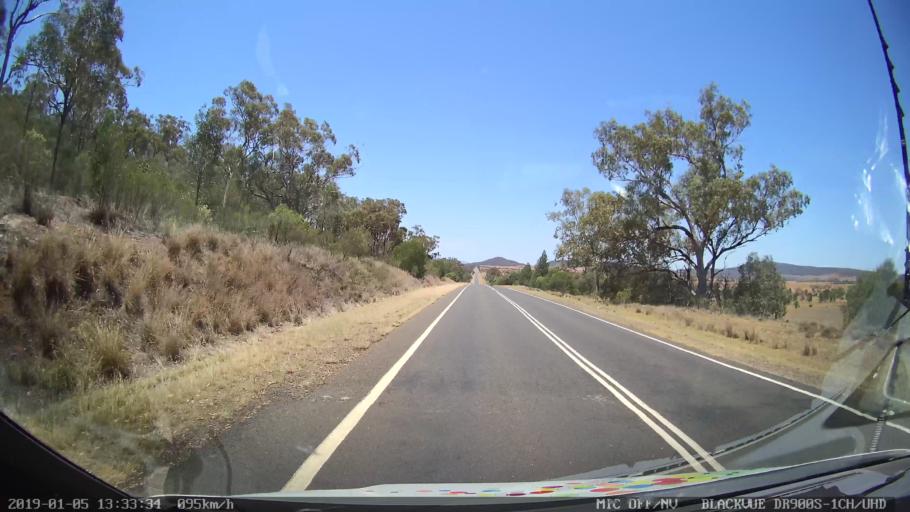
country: AU
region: New South Wales
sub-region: Gunnedah
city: Gunnedah
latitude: -31.0001
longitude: 150.1186
